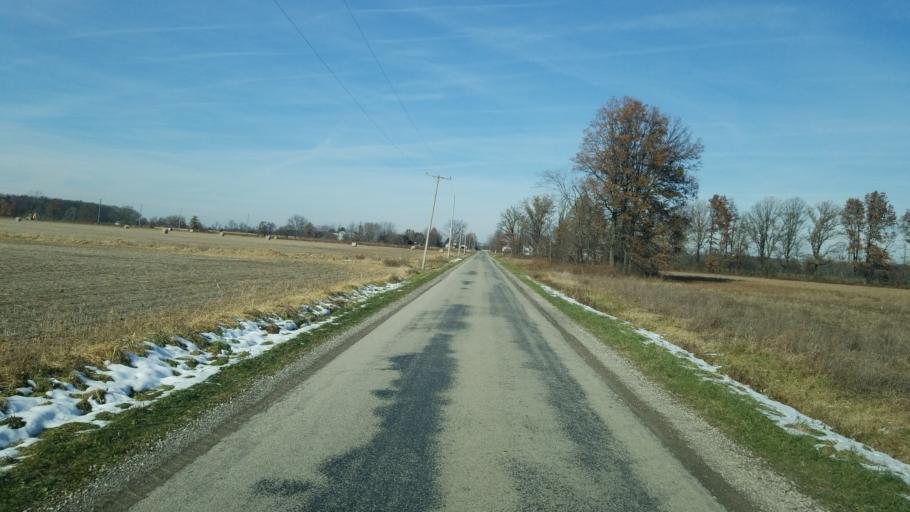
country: US
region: Ohio
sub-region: Huron County
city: Wakeman
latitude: 41.2324
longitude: -82.4194
